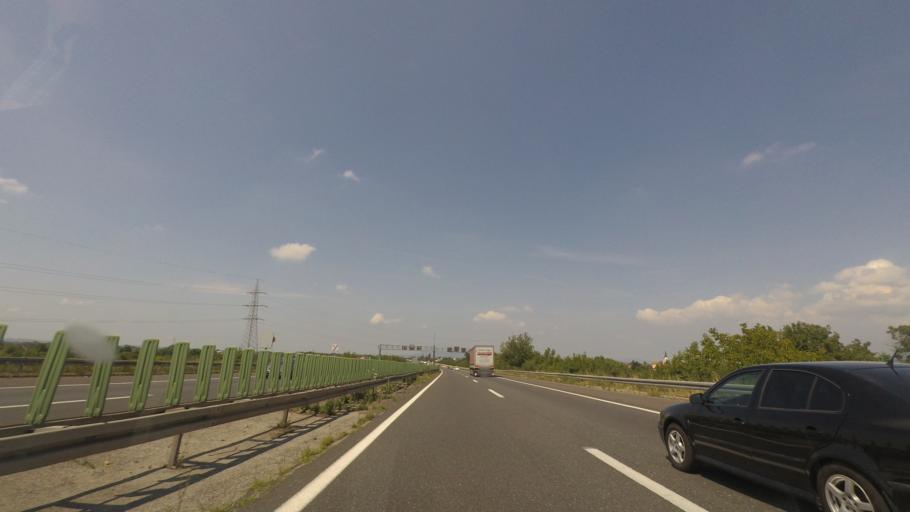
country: HR
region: Grad Zagreb
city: Odra
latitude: 45.7531
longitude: 15.9813
